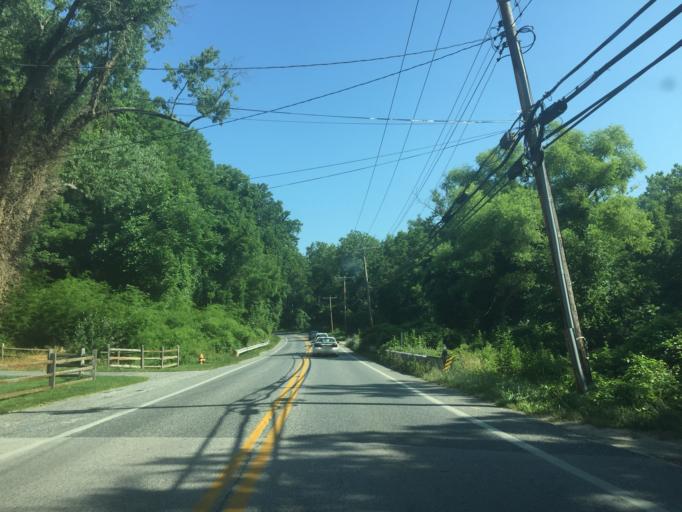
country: US
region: Maryland
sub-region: Baltimore County
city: Mays Chapel
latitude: 39.3877
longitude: -76.6594
